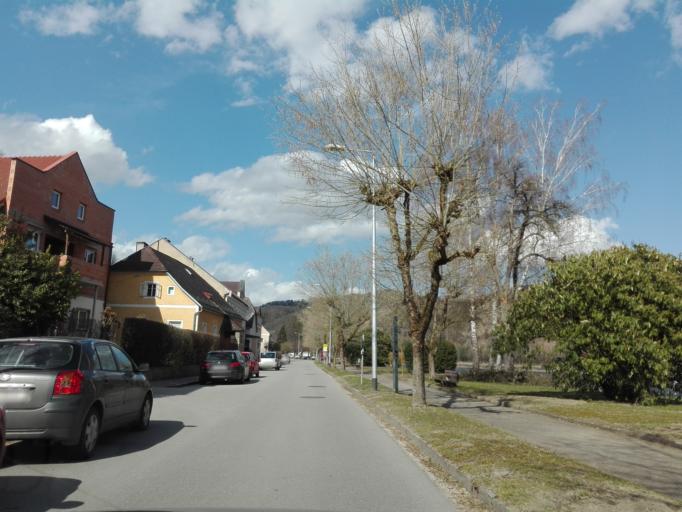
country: AT
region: Upper Austria
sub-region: Politischer Bezirk Urfahr-Umgebung
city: Feldkirchen an der Donau
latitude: 48.3708
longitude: 14.0277
